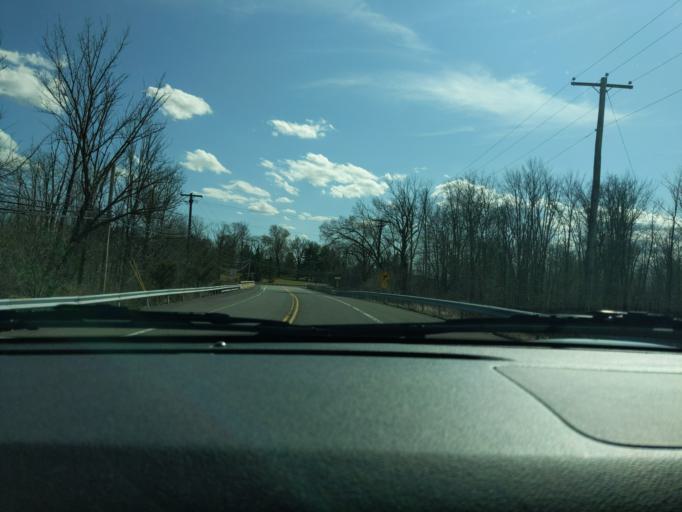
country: US
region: Pennsylvania
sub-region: Bucks County
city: Richlandtown
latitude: 40.4421
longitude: -75.3098
